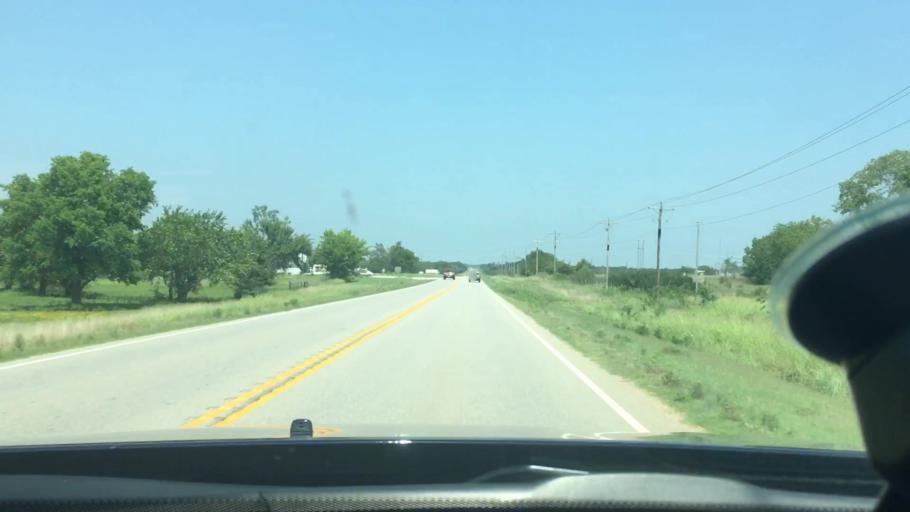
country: US
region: Oklahoma
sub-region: Coal County
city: Coalgate
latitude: 34.4791
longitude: -96.2181
